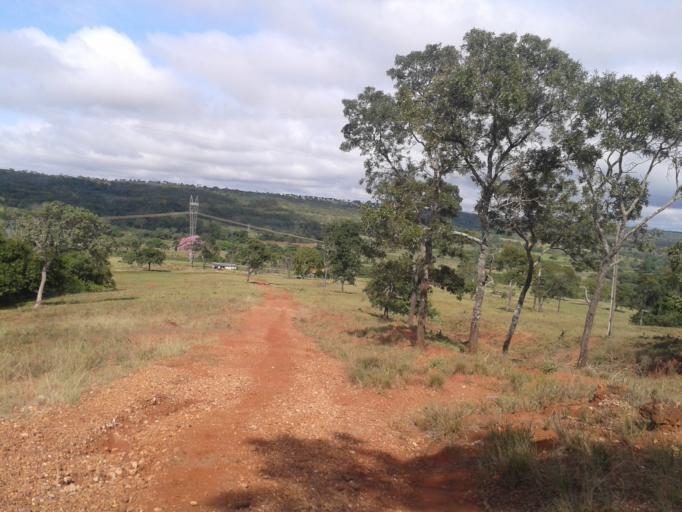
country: BR
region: Minas Gerais
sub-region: Campina Verde
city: Campina Verde
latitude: -19.4274
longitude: -49.6571
